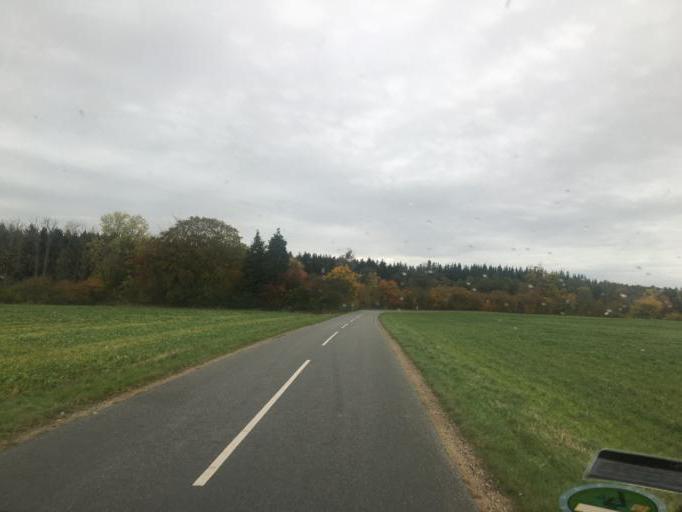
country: DK
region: Zealand
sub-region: Koge Kommune
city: Bjaeverskov
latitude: 55.4129
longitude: 11.9836
